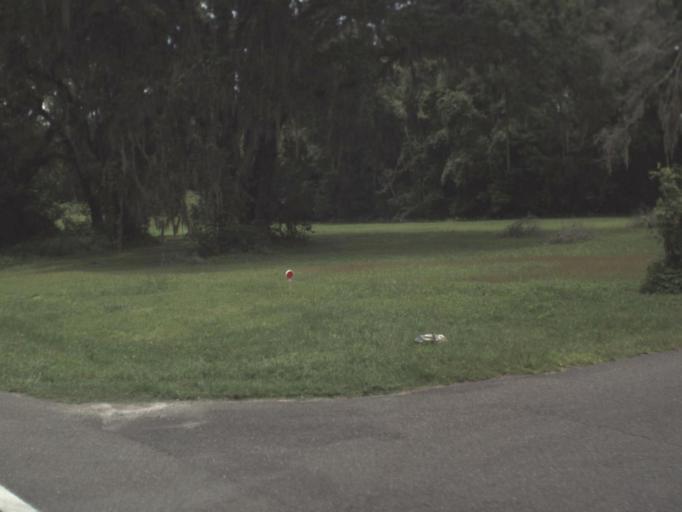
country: US
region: Florida
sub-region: Levy County
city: Williston
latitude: 29.4342
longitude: -82.4621
